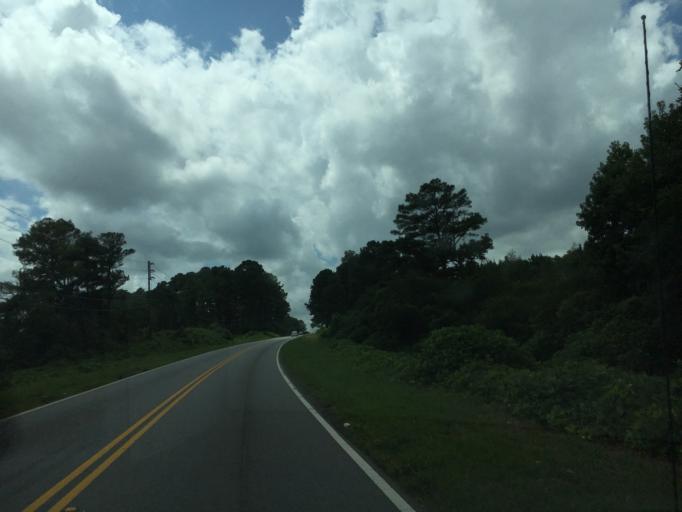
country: US
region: Georgia
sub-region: Rockdale County
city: Lakeview Estates
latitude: 33.6863
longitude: -84.0345
